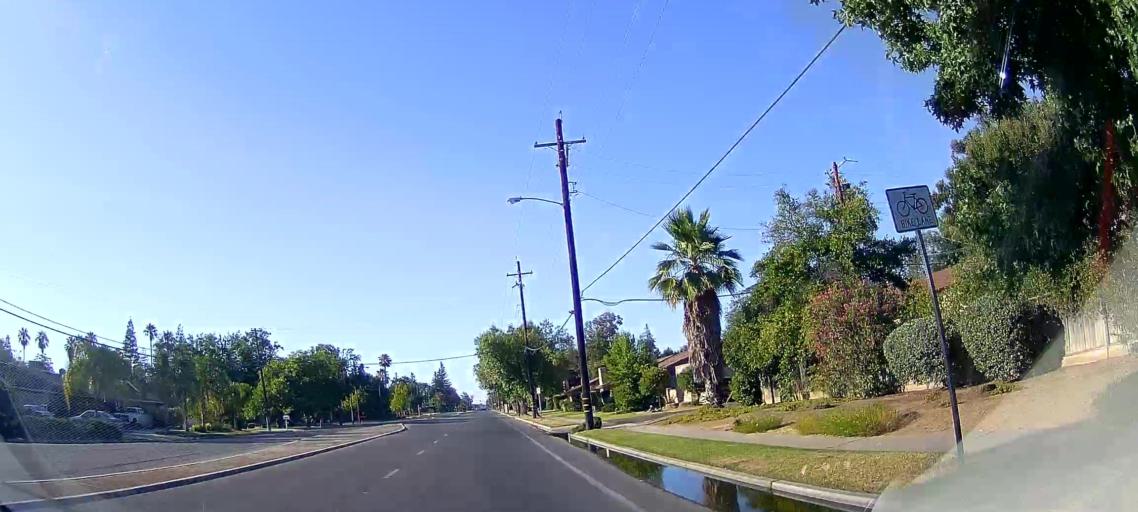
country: US
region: California
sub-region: Fresno County
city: Fresno
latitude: 36.8254
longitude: -119.8082
